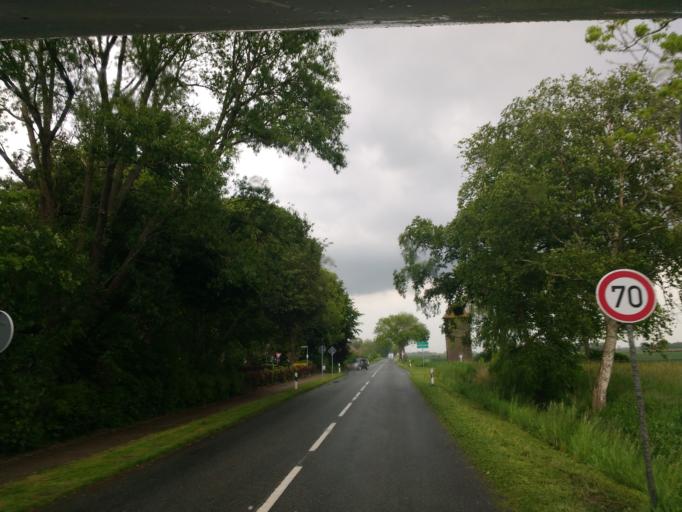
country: DE
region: Lower Saxony
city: Wangerooge
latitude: 53.6925
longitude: 7.8546
